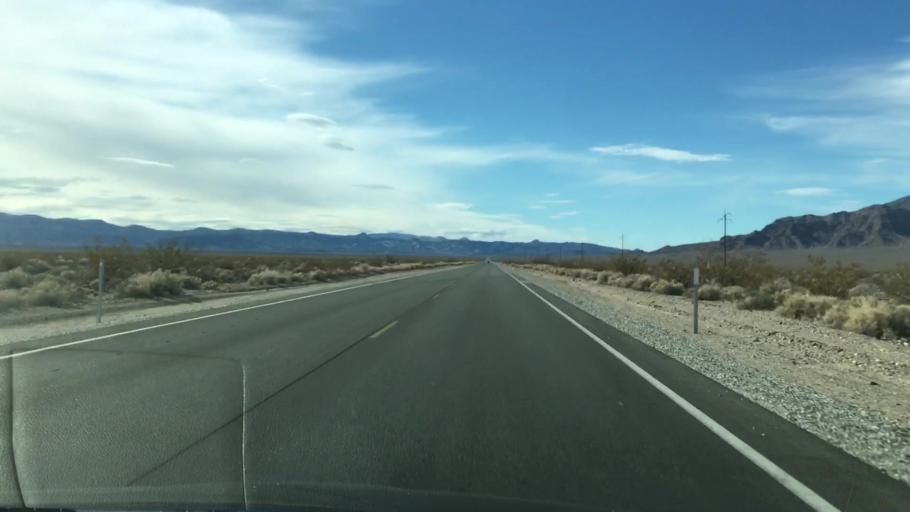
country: US
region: Nevada
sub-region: Nye County
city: Pahrump
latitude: 36.3042
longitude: -116.4298
